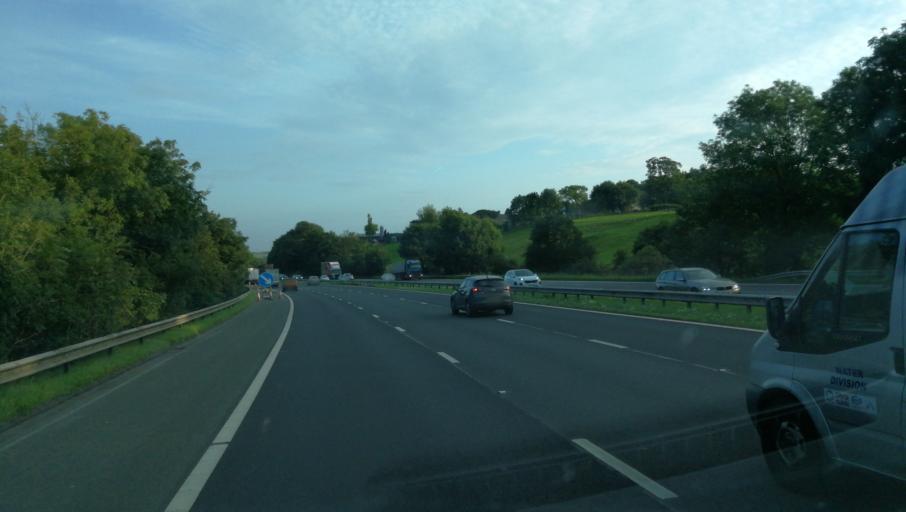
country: GB
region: England
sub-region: Lancashire
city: Bolton le Sands
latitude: 54.0909
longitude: -2.7671
